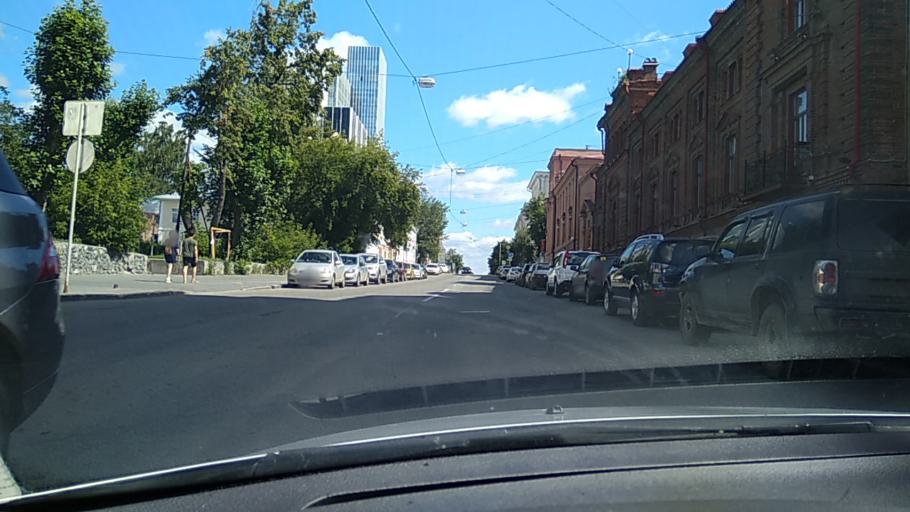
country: RU
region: Sverdlovsk
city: Yekaterinburg
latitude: 56.8422
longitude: 60.6116
